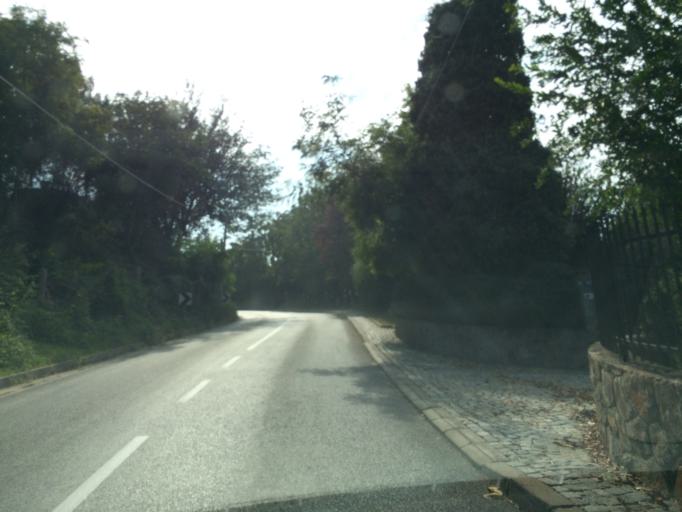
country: RS
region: Autonomna Pokrajina Vojvodina
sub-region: Juznobacki Okrug
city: Novi Sad
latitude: 45.2101
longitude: 19.8344
